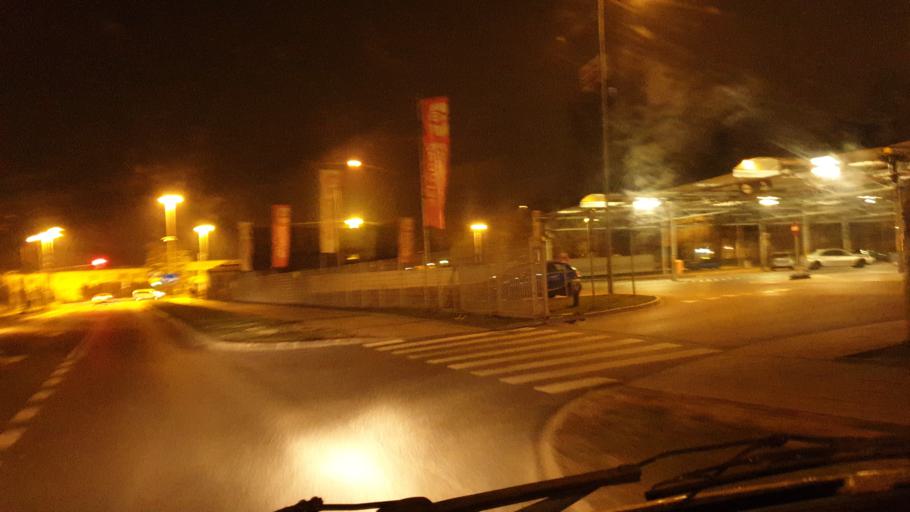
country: PL
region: Lodz Voivodeship
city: Lodz
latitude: 51.7186
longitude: 19.4401
